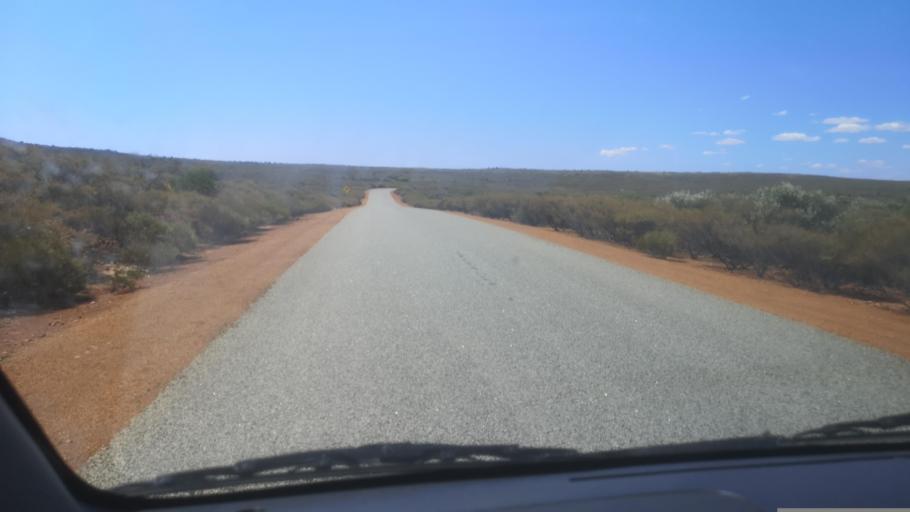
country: AU
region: Western Australia
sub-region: Northampton Shire
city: Kalbarri
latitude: -27.8144
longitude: 114.4710
